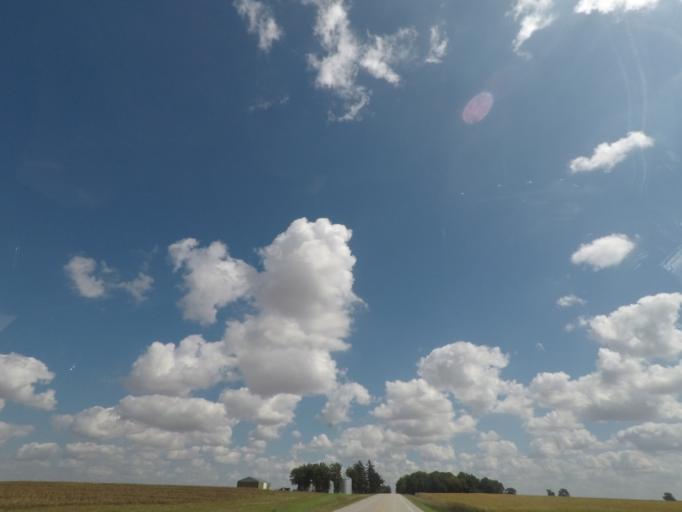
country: US
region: Iowa
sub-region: Story County
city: Nevada
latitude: 42.0779
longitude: -93.3813
